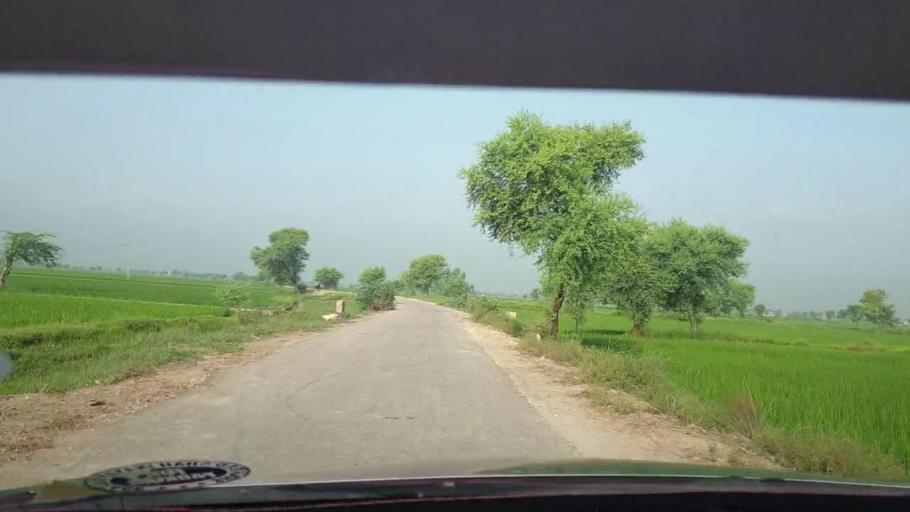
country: PK
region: Sindh
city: Goth Garelo
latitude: 27.4832
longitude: 68.0244
